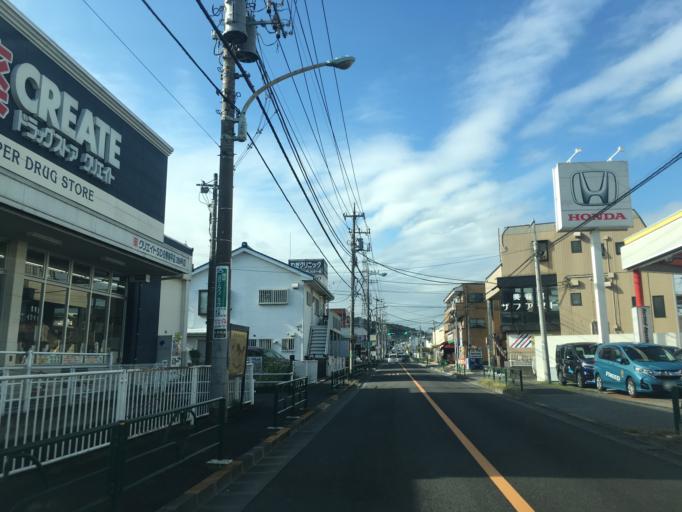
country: JP
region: Tokyo
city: Hino
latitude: 35.6524
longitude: 139.3917
